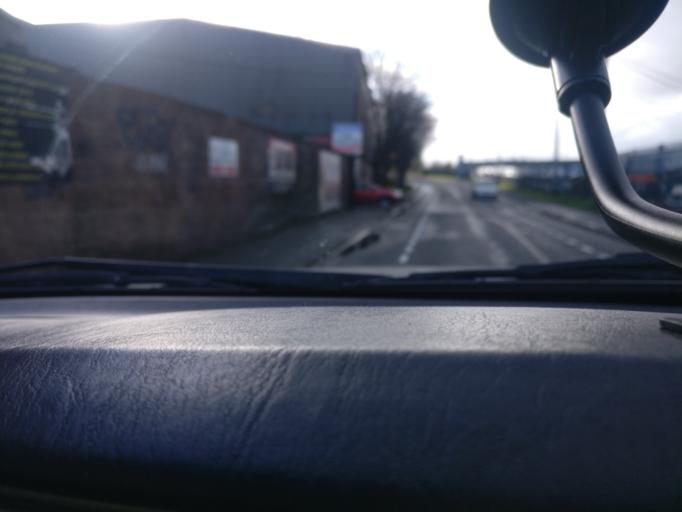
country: IE
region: Leinster
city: Crumlin
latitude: 53.3136
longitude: -6.3407
